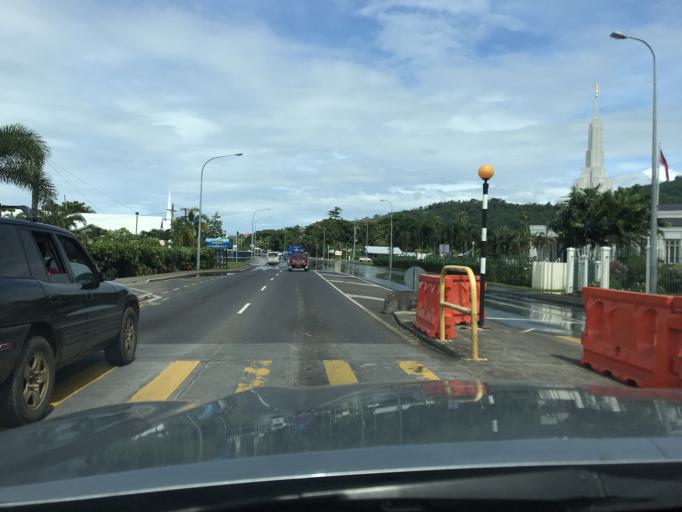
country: WS
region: Tuamasaga
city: Vaiusu
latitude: -13.8372
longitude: -171.7836
